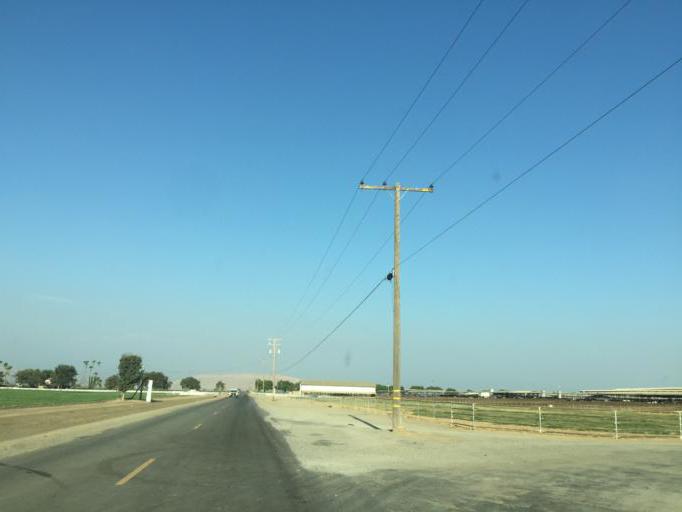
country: US
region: California
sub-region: Tulare County
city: Cutler
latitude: 36.4577
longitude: -119.2852
